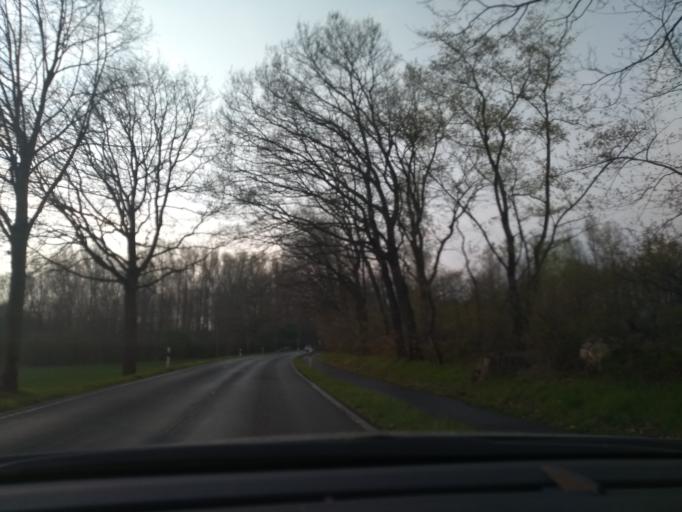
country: DE
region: North Rhine-Westphalia
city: Selm
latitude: 51.6421
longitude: 7.4676
